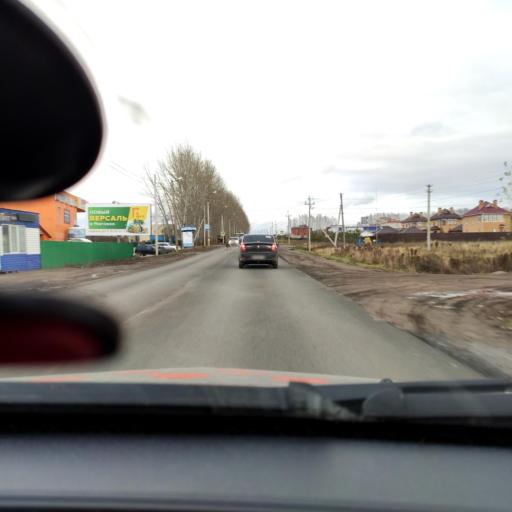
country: RU
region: Bashkortostan
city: Kabakovo
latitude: 54.6204
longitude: 56.1174
